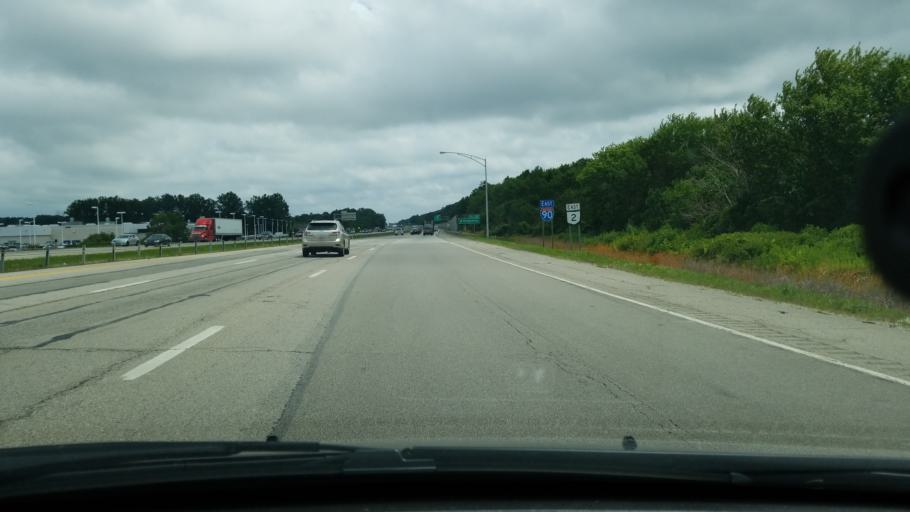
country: US
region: Ohio
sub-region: Lorain County
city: Avon
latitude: 41.4649
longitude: -82.0475
